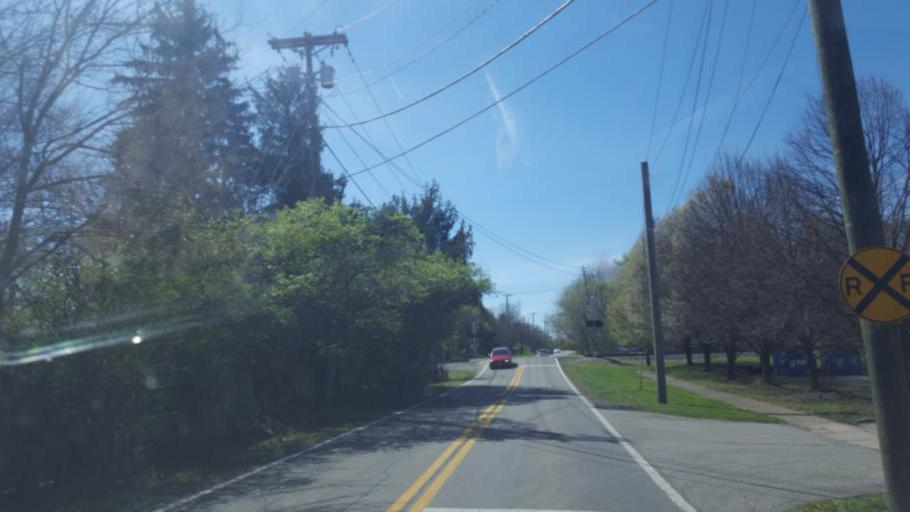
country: US
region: Ohio
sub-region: Franklin County
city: Worthington
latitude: 40.0825
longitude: -83.0499
